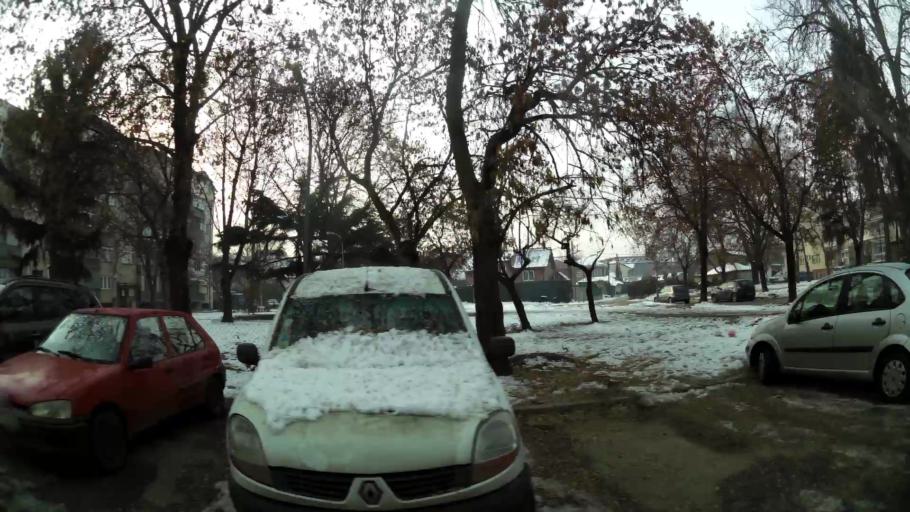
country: MK
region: Cair
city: Cair
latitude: 42.0177
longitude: 21.4418
